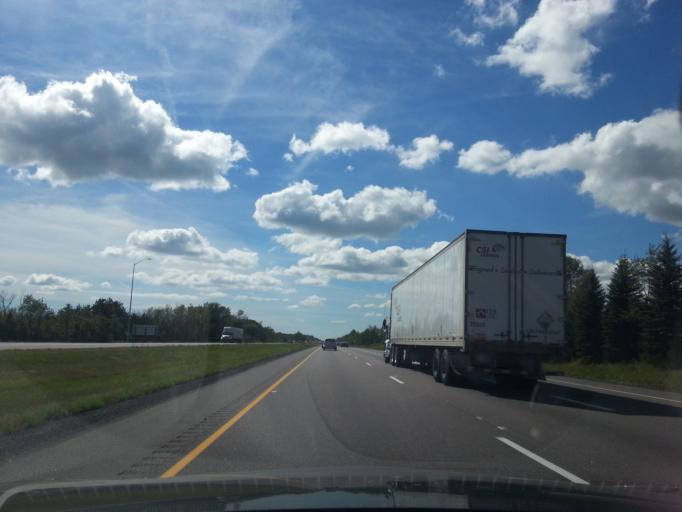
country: CA
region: Ontario
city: Deseronto
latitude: 44.2443
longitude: -77.0654
